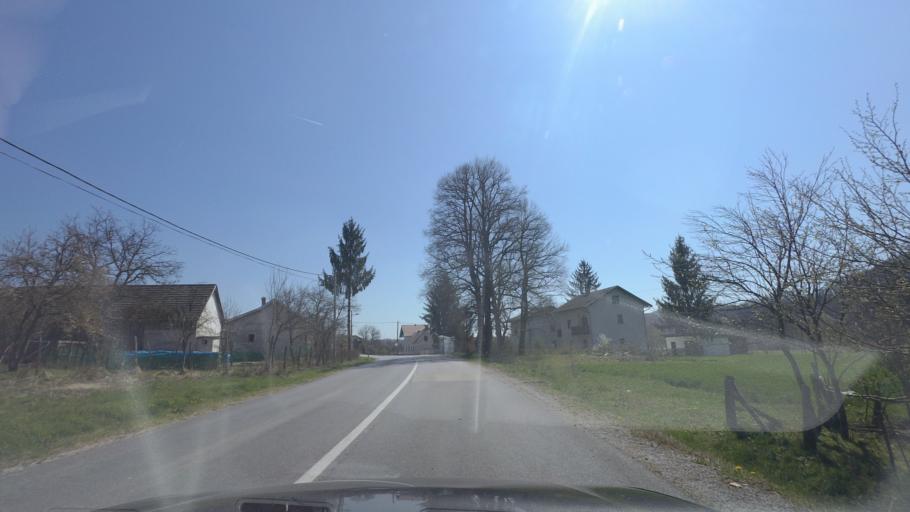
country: HR
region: Karlovacka
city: Vojnic
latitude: 45.3473
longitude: 15.6799
